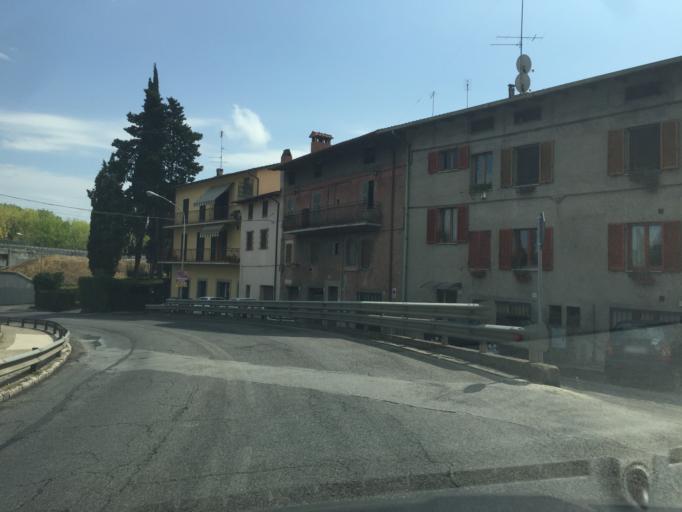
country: IT
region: Umbria
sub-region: Provincia di Perugia
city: Lacugnano
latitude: 43.1046
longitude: 12.3540
